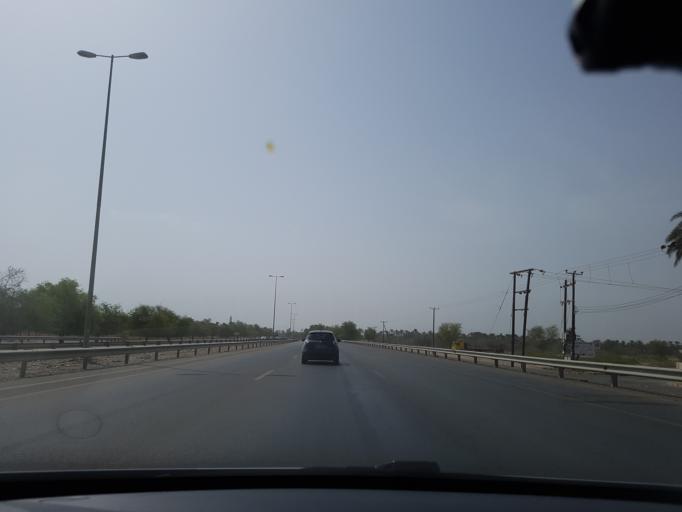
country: OM
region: Al Batinah
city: Al Khaburah
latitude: 23.9560
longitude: 57.1030
